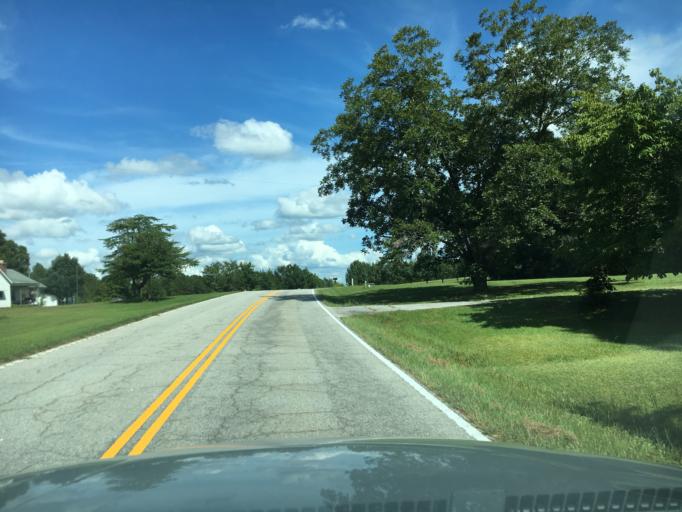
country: US
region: South Carolina
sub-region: Greenwood County
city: Ware Shoals
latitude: 34.4658
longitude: -82.1804
